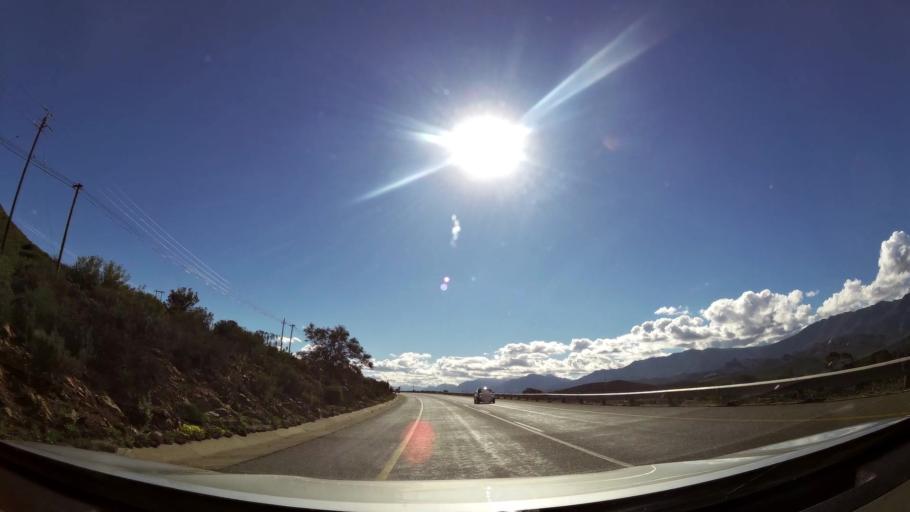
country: ZA
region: Western Cape
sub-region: Cape Winelands District Municipality
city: Ashton
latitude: -33.7796
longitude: 19.7656
